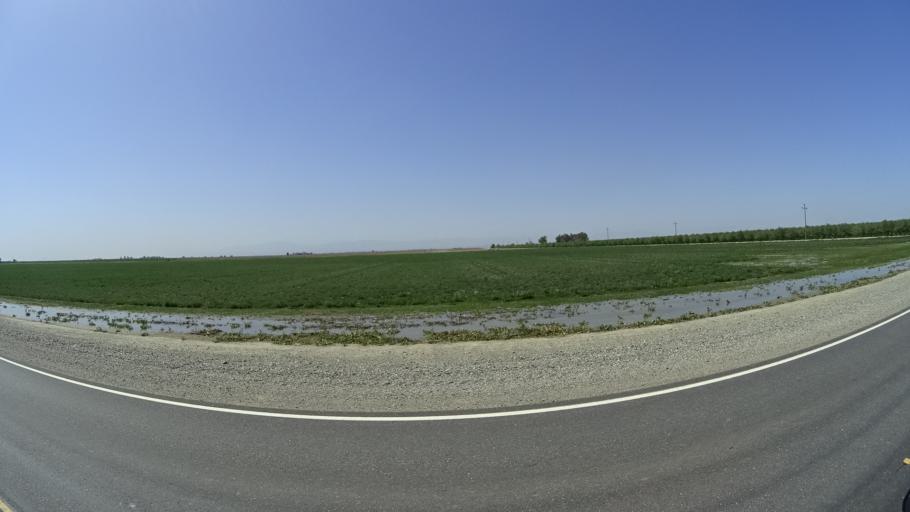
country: US
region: California
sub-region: Glenn County
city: Willows
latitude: 39.5956
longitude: -122.1372
